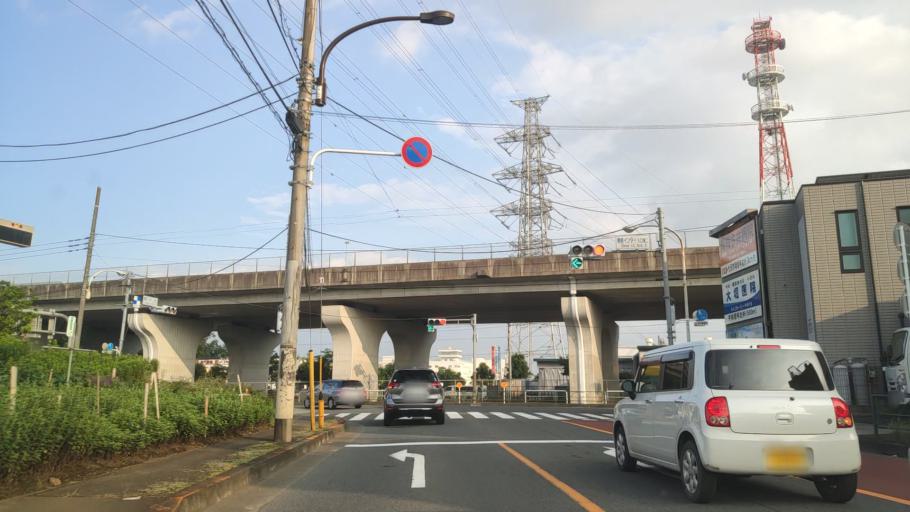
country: JP
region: Saitama
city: Hanno
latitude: 35.7962
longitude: 139.3174
